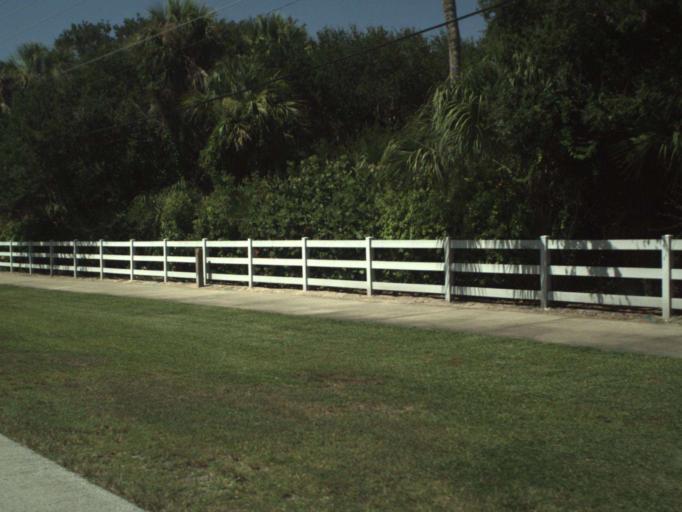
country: US
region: Florida
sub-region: Indian River County
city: South Beach
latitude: 27.5976
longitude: -80.3355
